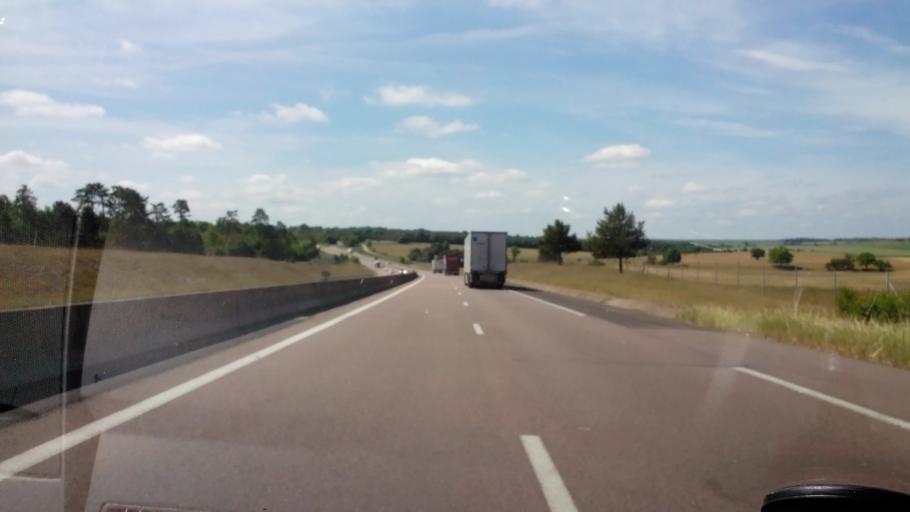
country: FR
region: Lorraine
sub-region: Departement de Meurthe-et-Moselle
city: Colombey-les-Belles
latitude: 48.4375
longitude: 5.8627
